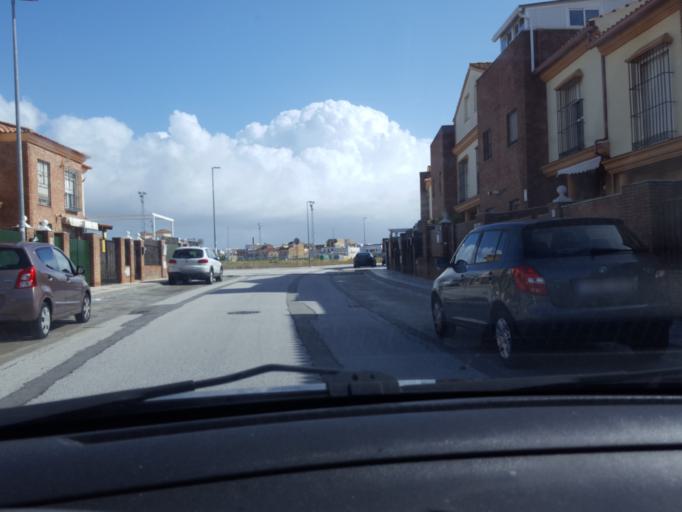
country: ES
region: Andalusia
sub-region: Provincia de Sevilla
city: Acala del Rio
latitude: 37.5151
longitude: -5.9883
